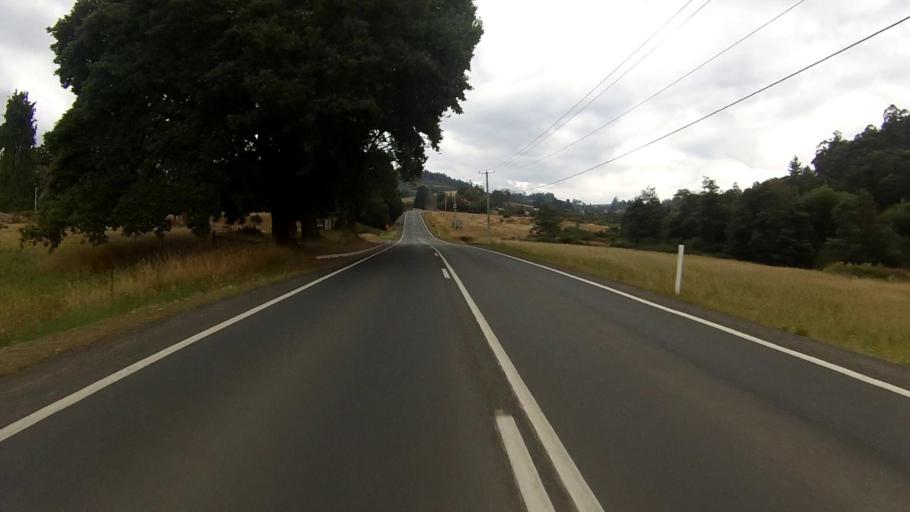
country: AU
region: Tasmania
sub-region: Huon Valley
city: Cygnet
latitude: -43.1397
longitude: 147.0608
